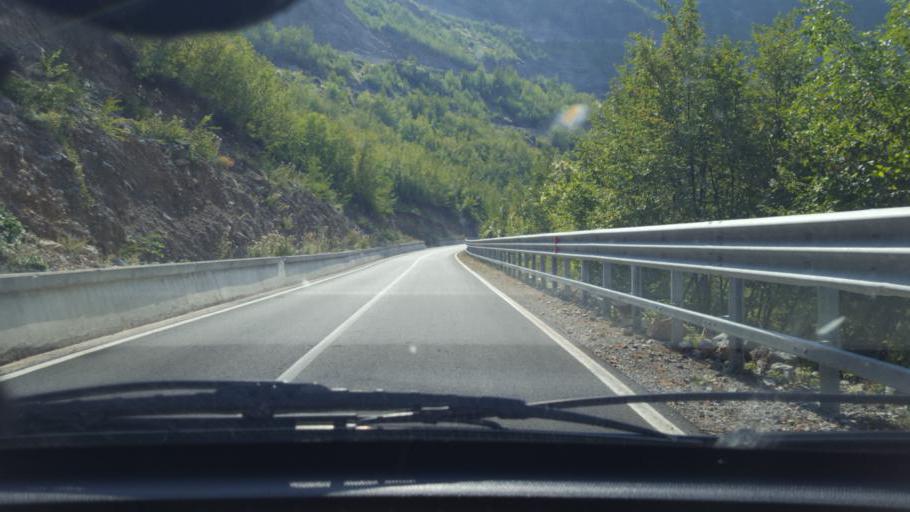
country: AL
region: Shkoder
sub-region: Rrethi i Malesia e Madhe
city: Kastrat
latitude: 42.4161
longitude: 19.5017
